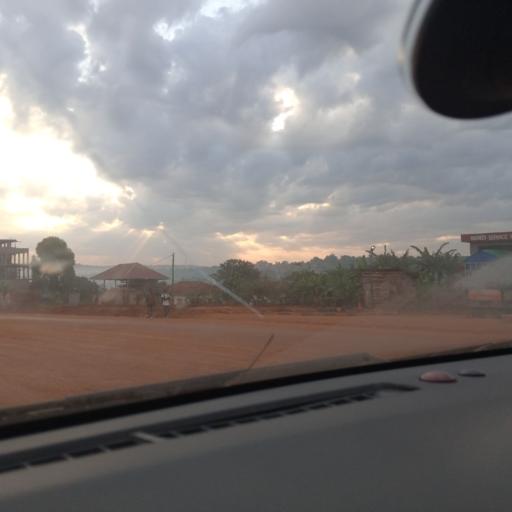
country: UG
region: Central Region
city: Masaka
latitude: -0.3357
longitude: 31.7407
